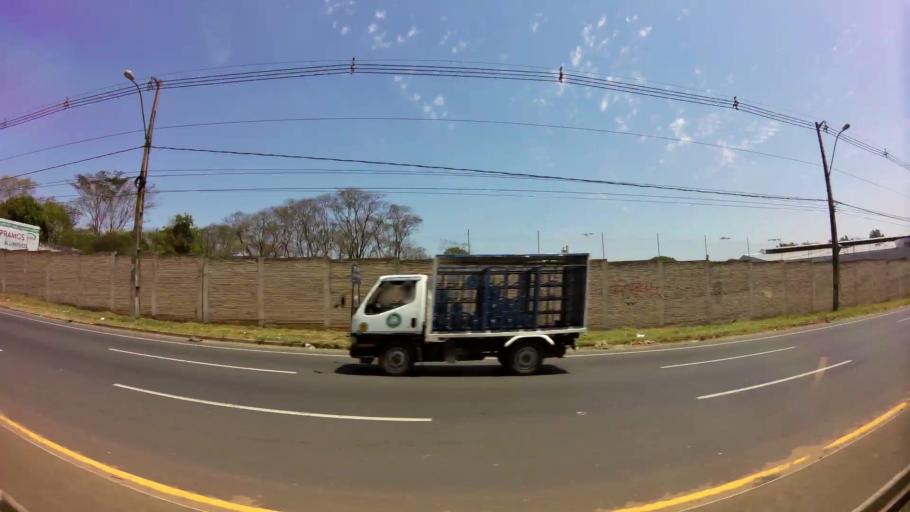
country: PY
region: Central
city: Villa Elisa
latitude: -25.3621
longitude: -57.5659
